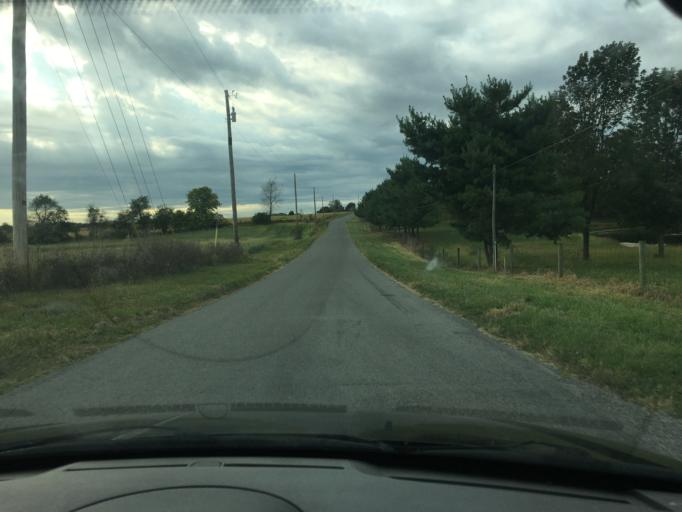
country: US
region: Ohio
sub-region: Logan County
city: Bellefontaine
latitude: 40.3340
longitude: -83.7952
